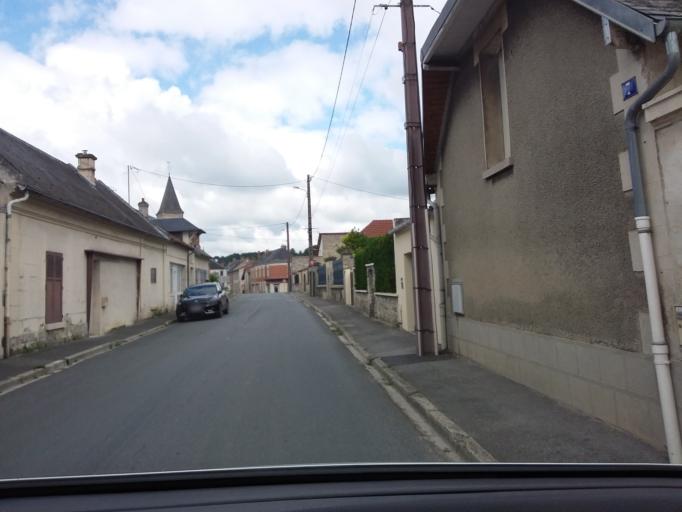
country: FR
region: Picardie
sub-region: Departement de l'Aisne
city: Vailly-sur-Aisne
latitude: 49.4095
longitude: 3.5204
